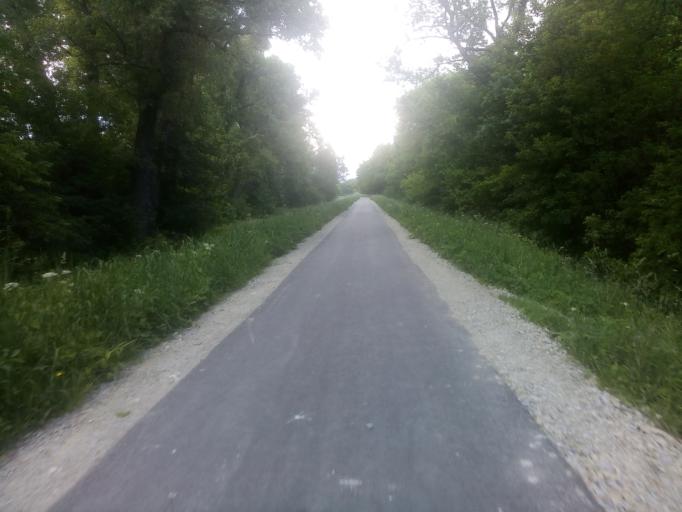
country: PL
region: Lesser Poland Voivodeship
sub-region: Powiat nowosadecki
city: Nowy Sacz
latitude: 49.6192
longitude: 20.6849
